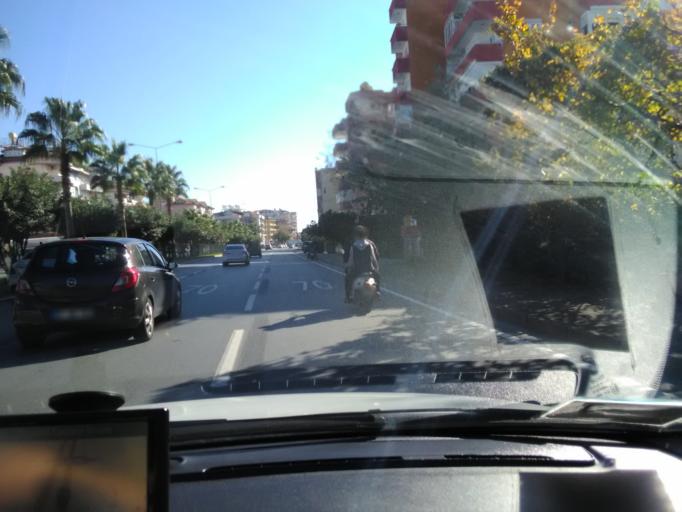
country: TR
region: Antalya
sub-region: Alanya
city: Alanya
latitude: 36.5355
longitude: 32.0443
